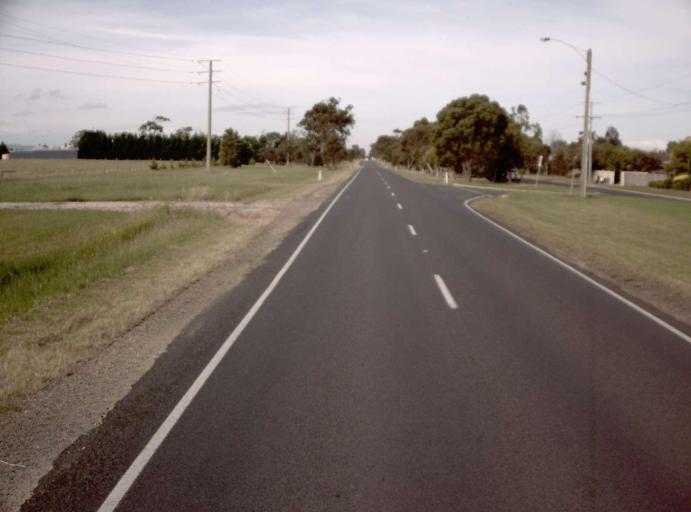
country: AU
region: Victoria
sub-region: Latrobe
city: Traralgon
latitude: -38.1259
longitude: 146.5674
